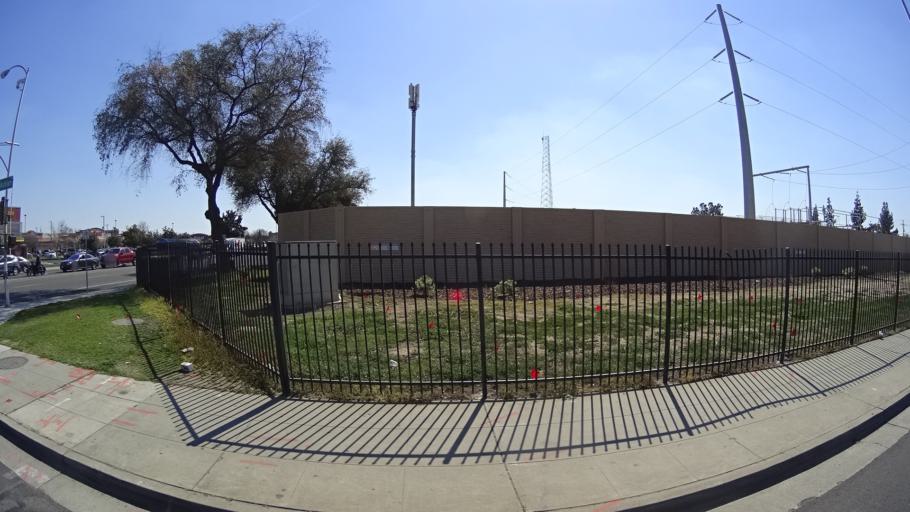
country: US
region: California
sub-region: Fresno County
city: Fresno
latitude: 36.7935
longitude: -119.8267
